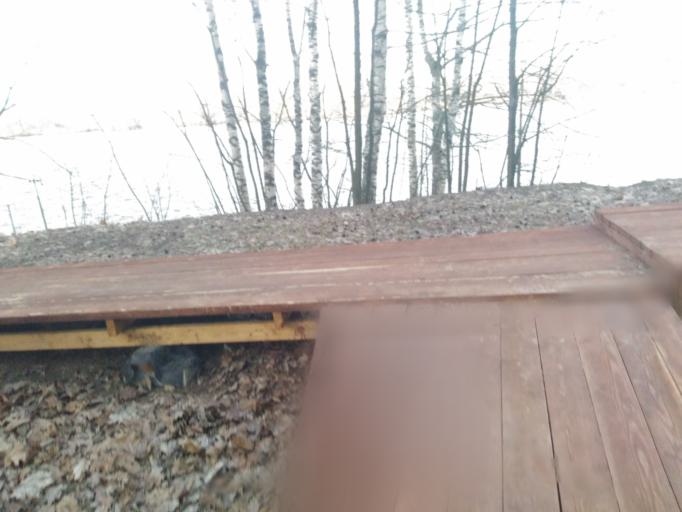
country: RU
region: Moscow
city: Shchukino
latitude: 55.7862
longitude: 37.4217
